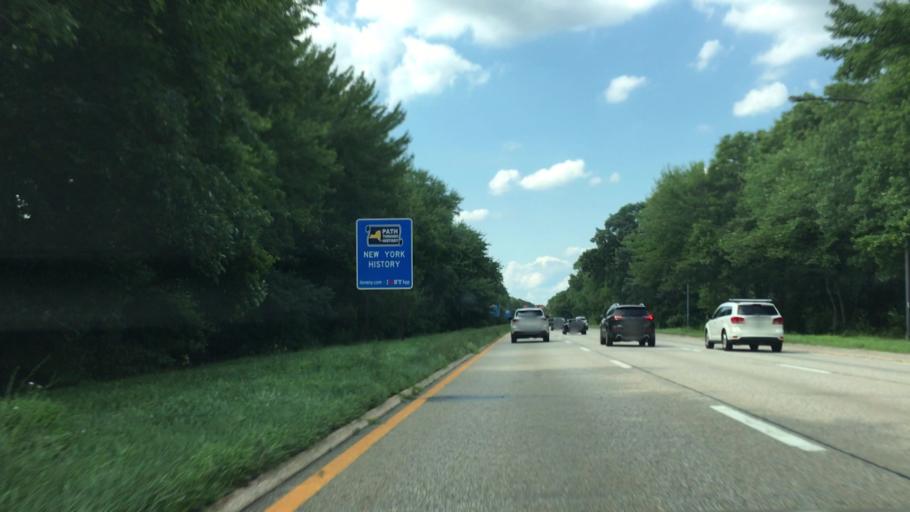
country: US
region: New York
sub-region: Nassau County
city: Freeport
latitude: 40.6720
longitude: -73.5698
